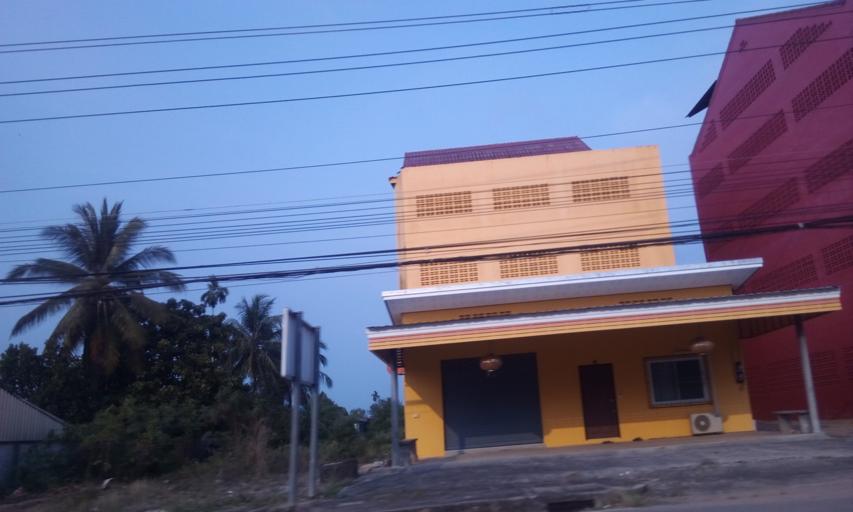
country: TH
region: Trat
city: Khao Saming
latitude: 12.3845
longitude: 102.3720
